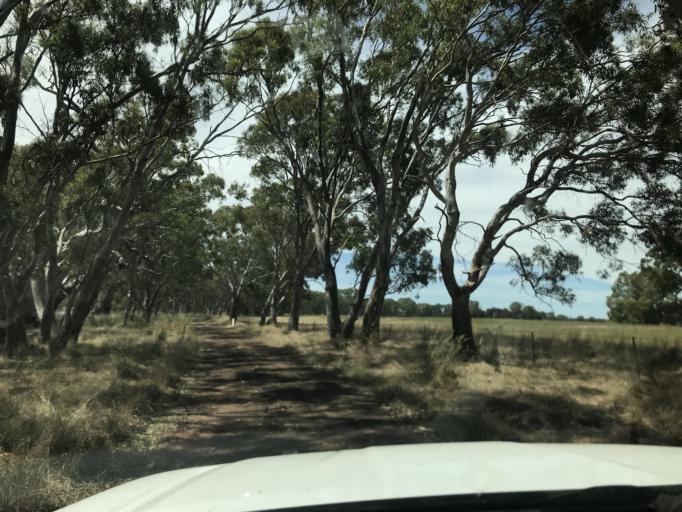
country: AU
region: South Australia
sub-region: Wattle Range
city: Penola
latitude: -37.0002
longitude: 141.4943
